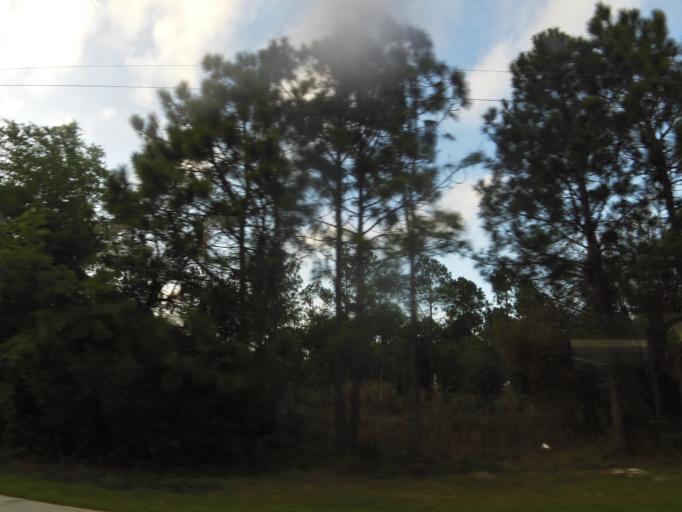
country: US
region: Florida
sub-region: Duval County
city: Jacksonville
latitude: 30.4394
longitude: -81.6060
